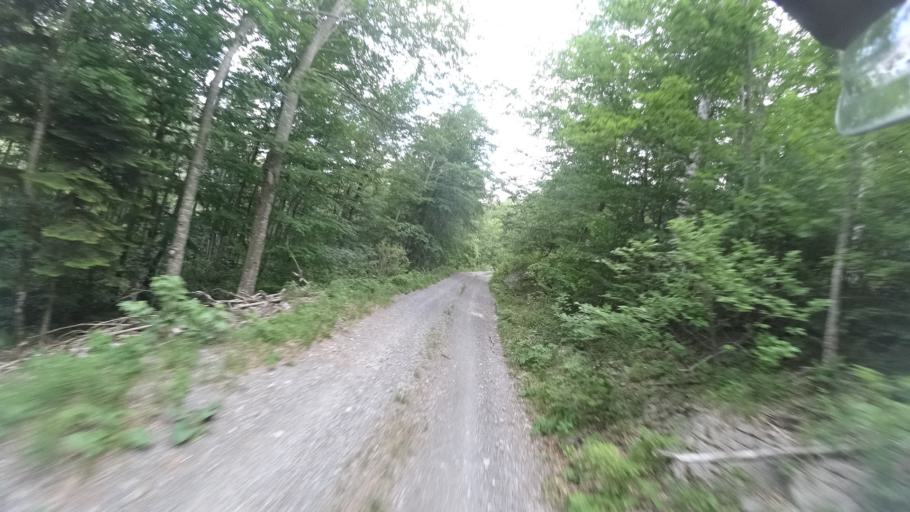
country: HR
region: Licko-Senjska
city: Gospic
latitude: 44.4442
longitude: 15.3006
